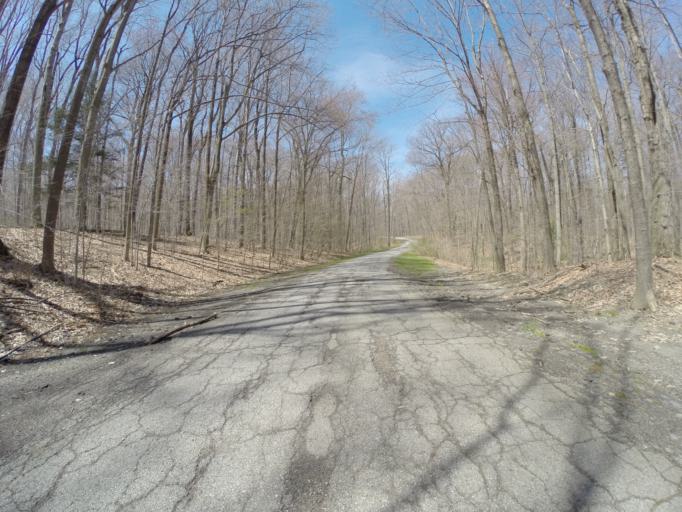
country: US
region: Ohio
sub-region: Cuyahoga County
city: Mayfield
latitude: 41.5528
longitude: -81.4243
